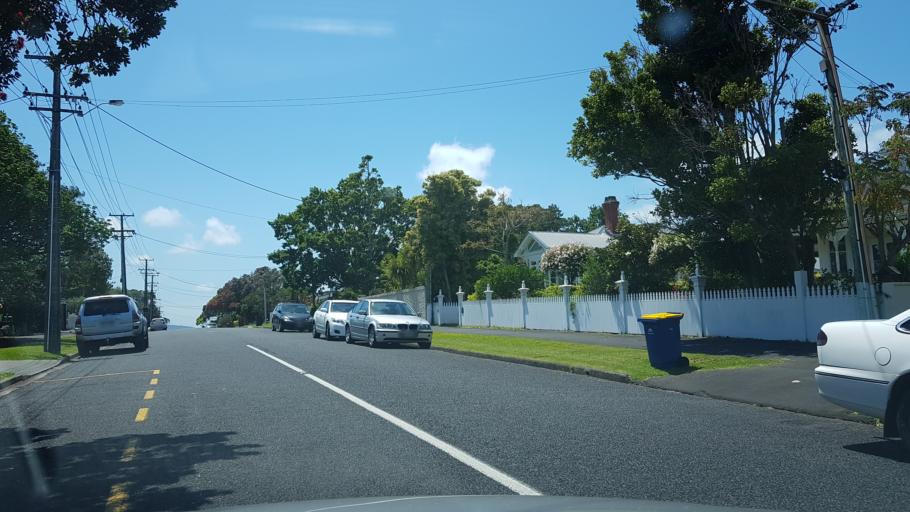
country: NZ
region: Auckland
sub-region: Auckland
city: North Shore
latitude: -36.8267
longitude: 174.7755
